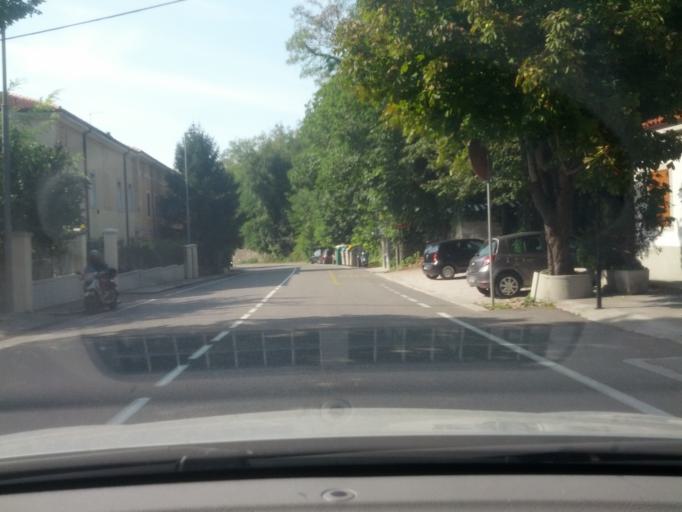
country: IT
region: Friuli Venezia Giulia
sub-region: Provincia di Trieste
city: Trieste
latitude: 45.6611
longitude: 13.8077
